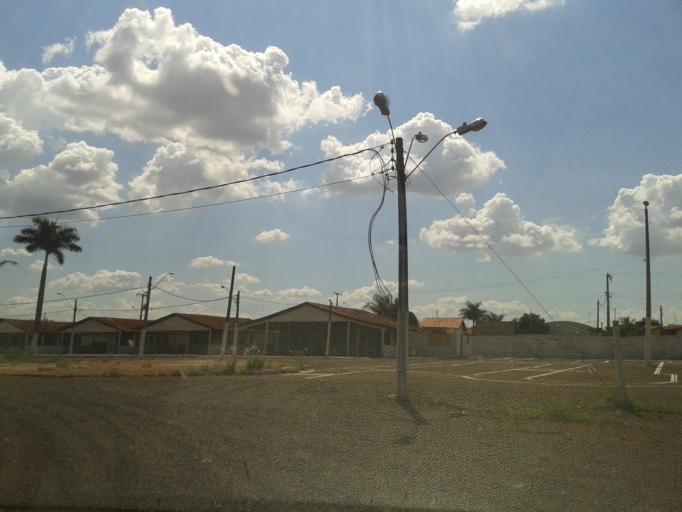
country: BR
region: Minas Gerais
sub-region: Centralina
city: Centralina
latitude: -18.7265
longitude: -49.1935
